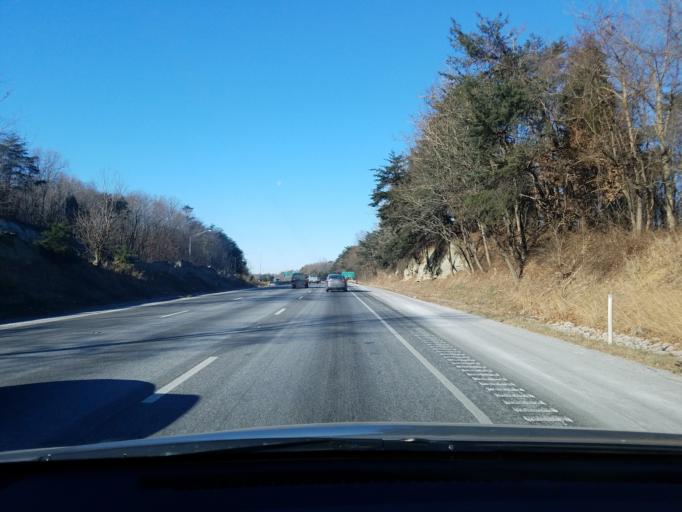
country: US
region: Indiana
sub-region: Floyd County
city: New Albany
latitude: 38.3040
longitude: -85.8803
